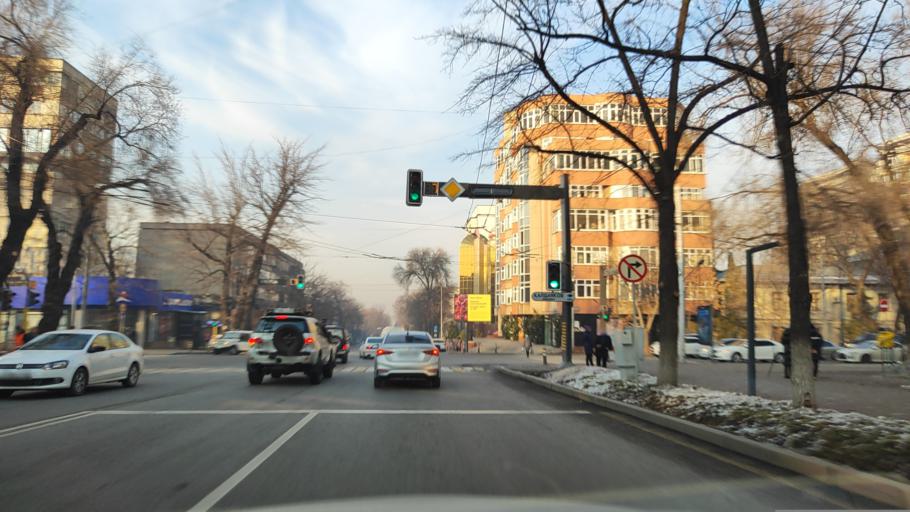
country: KZ
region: Almaty Qalasy
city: Almaty
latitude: 43.2534
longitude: 76.9557
